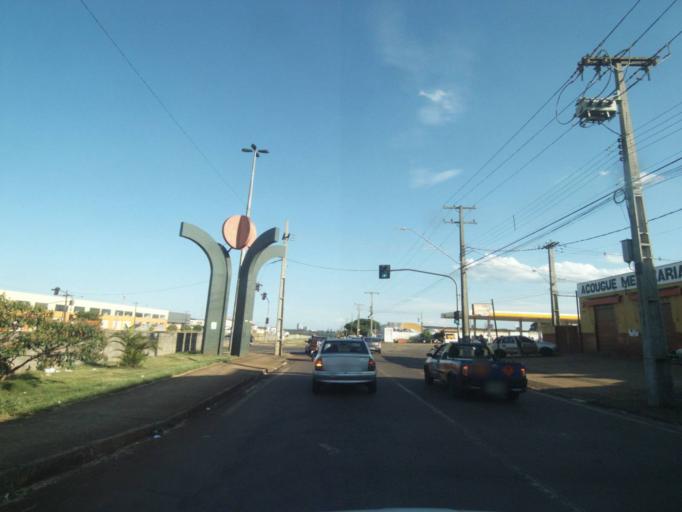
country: BR
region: Parana
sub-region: Londrina
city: Londrina
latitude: -23.3118
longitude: -51.2169
